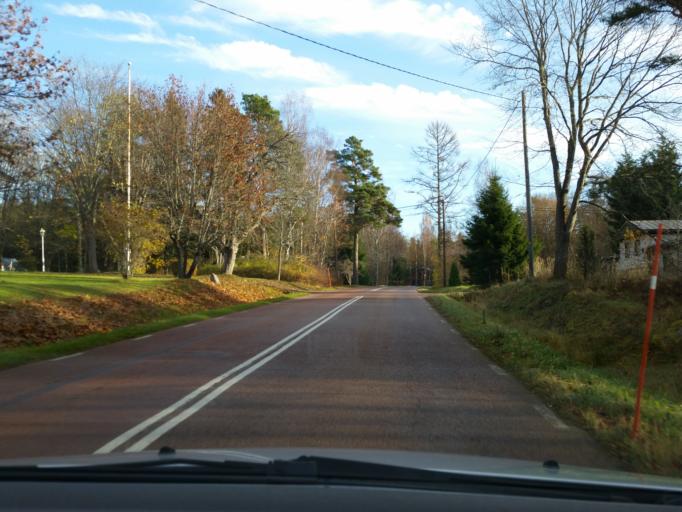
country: AX
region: Alands landsbygd
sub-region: Saltvik
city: Saltvik
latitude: 60.3206
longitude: 20.0410
